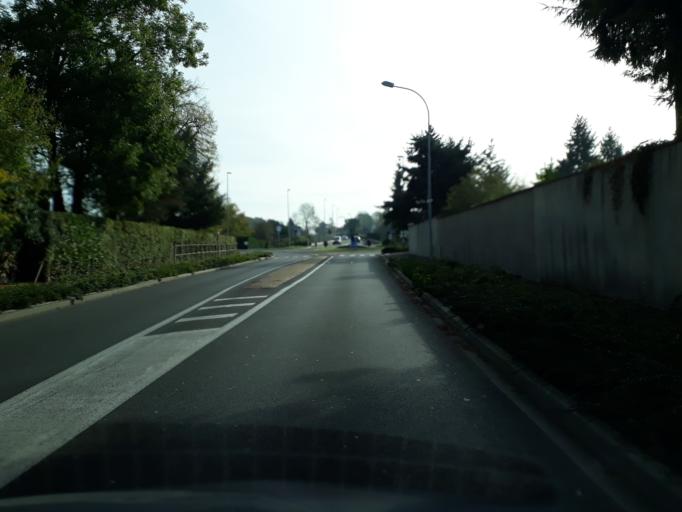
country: FR
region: Ile-de-France
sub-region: Departement de Seine-et-Marne
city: Samoreau
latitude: 48.4288
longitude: 2.7498
